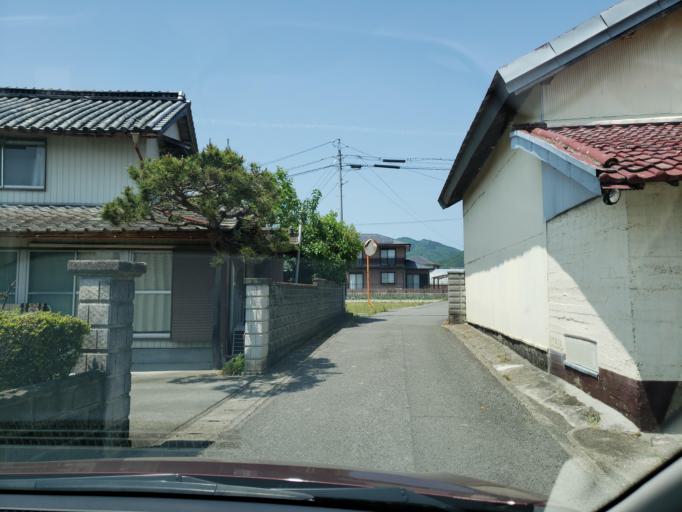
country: JP
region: Tokushima
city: Kamojimacho-jogejima
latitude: 34.0955
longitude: 134.2682
